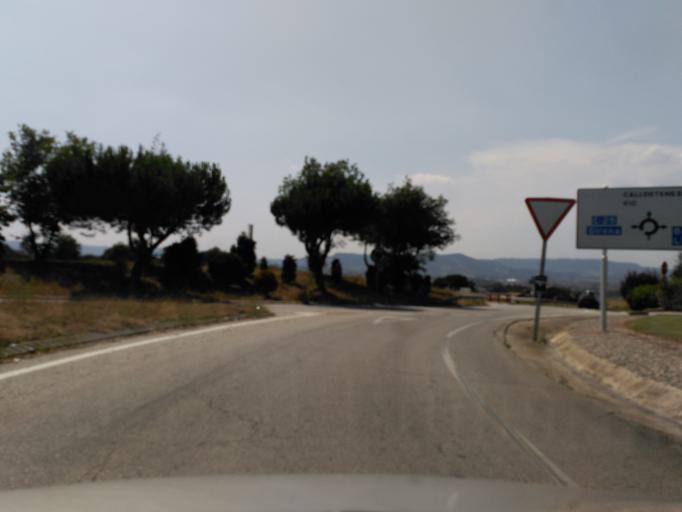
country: ES
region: Catalonia
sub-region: Provincia de Barcelona
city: Sant Julia de Vilatorta
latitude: 41.9292
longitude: 2.3018
